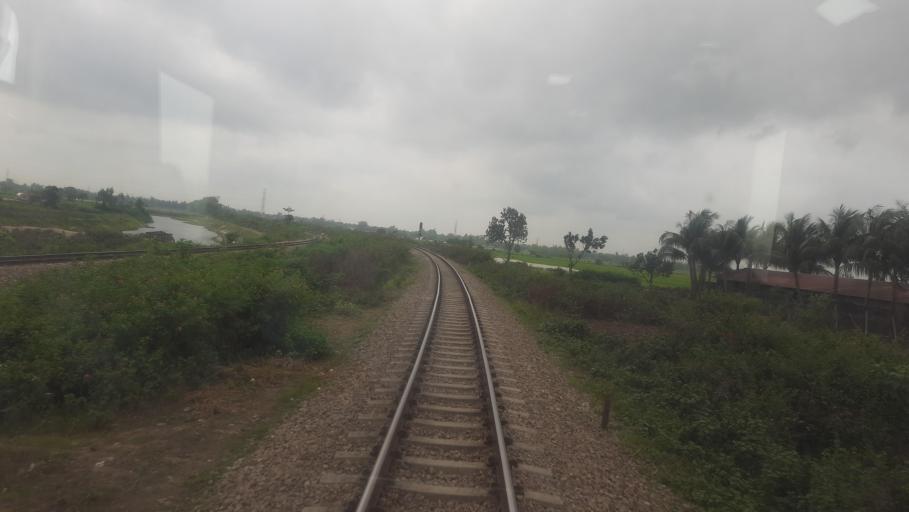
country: BD
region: Dhaka
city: Bhairab Bazar
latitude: 24.0489
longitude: 90.9688
